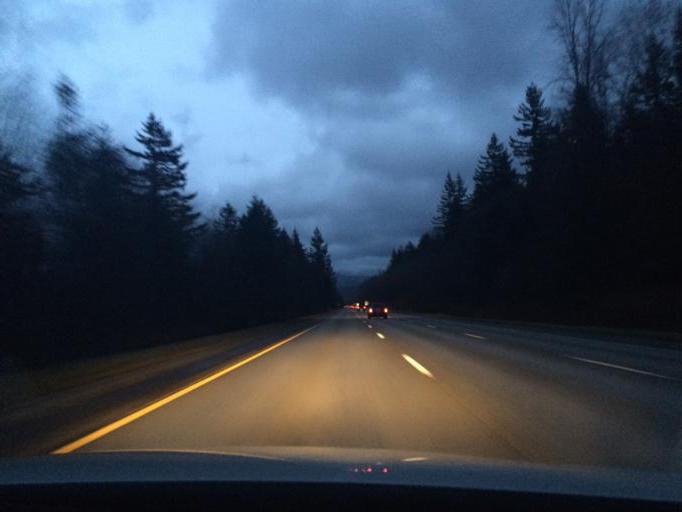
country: US
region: Washington
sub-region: King County
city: Snoqualmie
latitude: 47.5115
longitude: -121.8322
